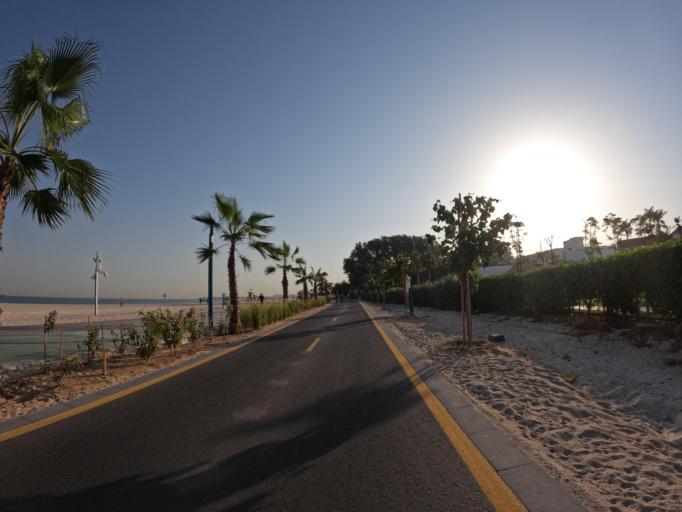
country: AE
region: Dubai
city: Dubai
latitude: 25.1801
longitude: 55.2212
